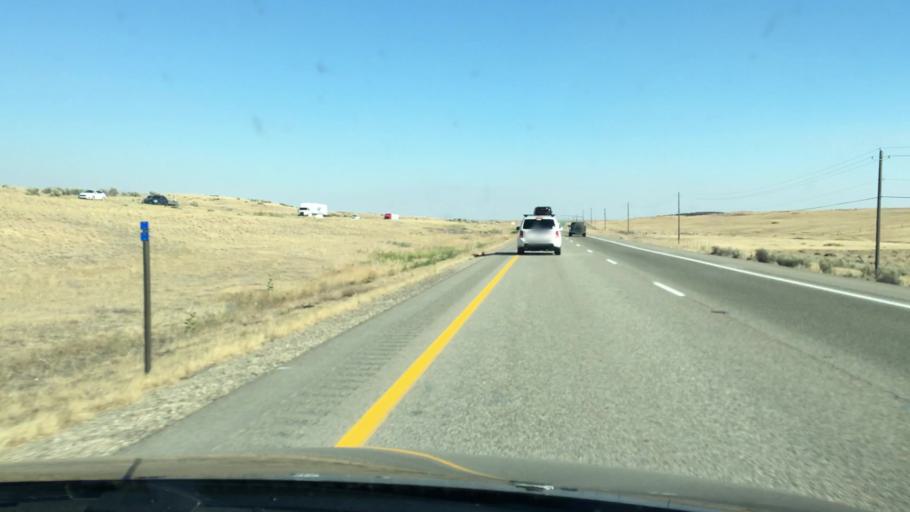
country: US
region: Idaho
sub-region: Ada County
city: Boise
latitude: 43.4447
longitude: -116.0727
